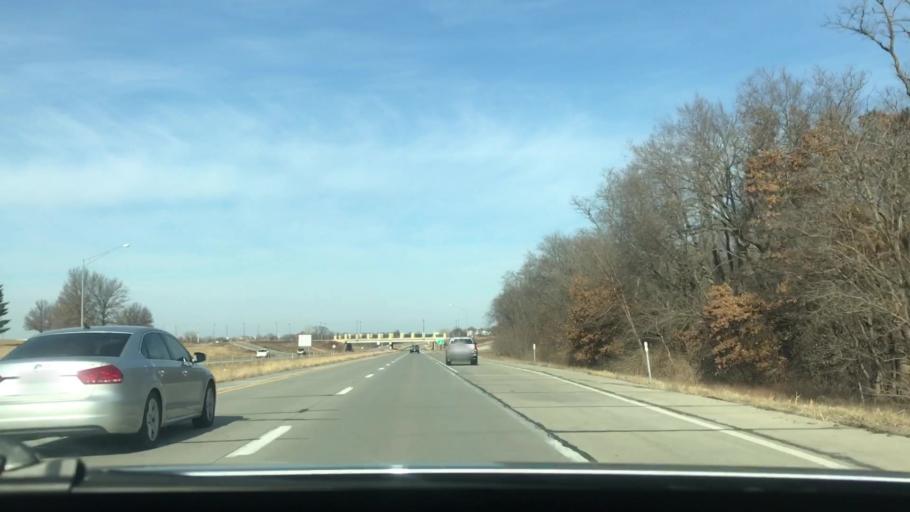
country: US
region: Missouri
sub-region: Clay County
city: Gladstone
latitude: 39.2847
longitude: -94.5850
